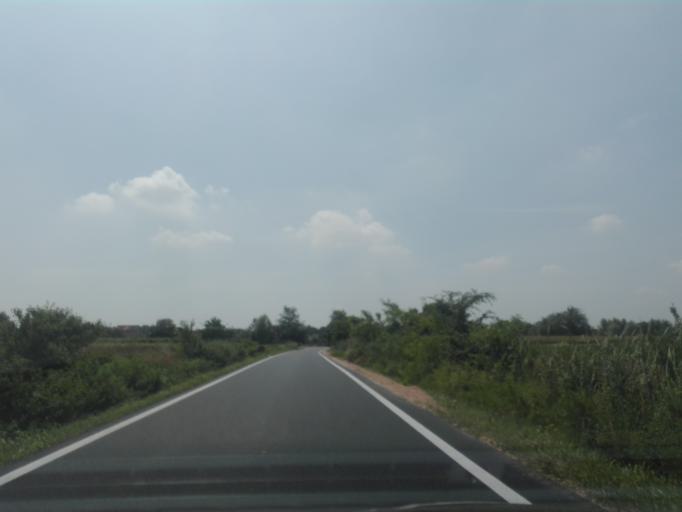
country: IT
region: Veneto
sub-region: Provincia di Rovigo
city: Grignano Polesine
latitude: 45.0513
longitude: 11.7513
